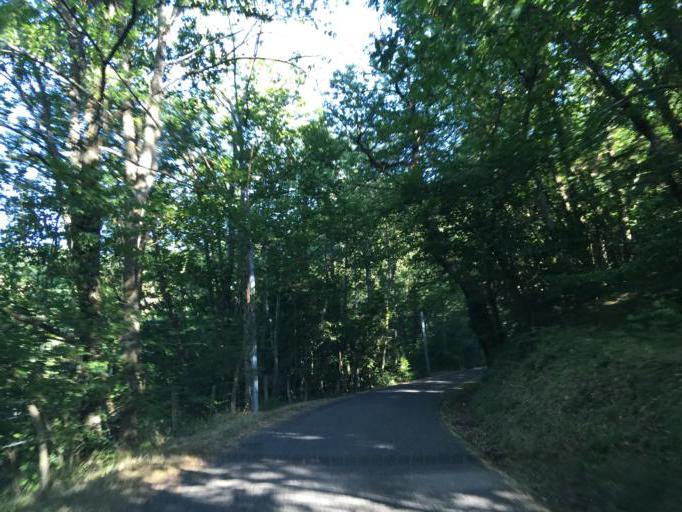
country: FR
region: Rhone-Alpes
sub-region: Departement de la Loire
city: Saint-Jean-Bonnefonds
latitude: 45.4320
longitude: 4.4735
